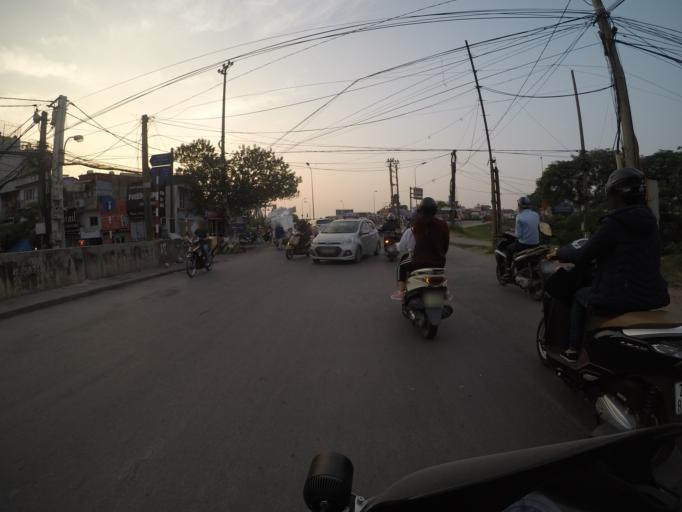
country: VN
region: Ha Noi
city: Hoan Kiem
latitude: 21.0393
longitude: 105.8664
